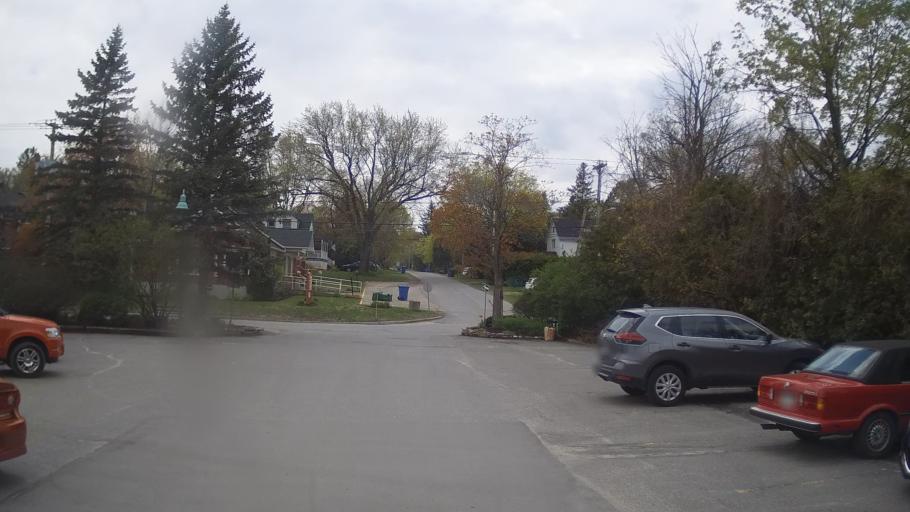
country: CA
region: Quebec
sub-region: Monteregie
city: Hudson
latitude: 45.4597
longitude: -74.1429
